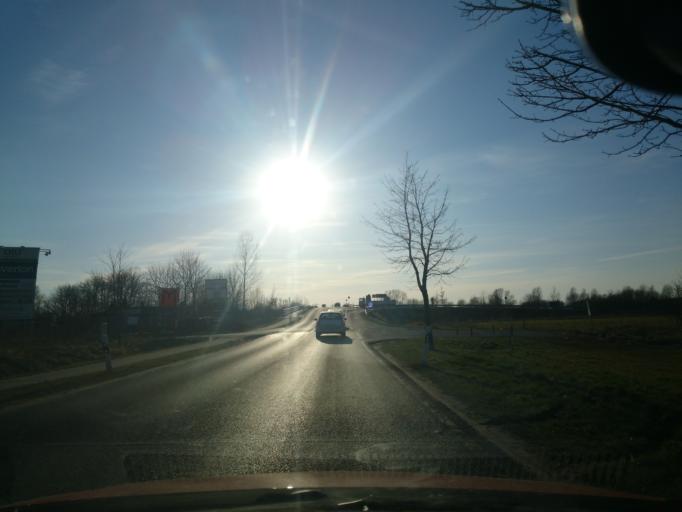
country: DE
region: Mecklenburg-Vorpommern
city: Greifswald
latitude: 54.0904
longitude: 13.3472
